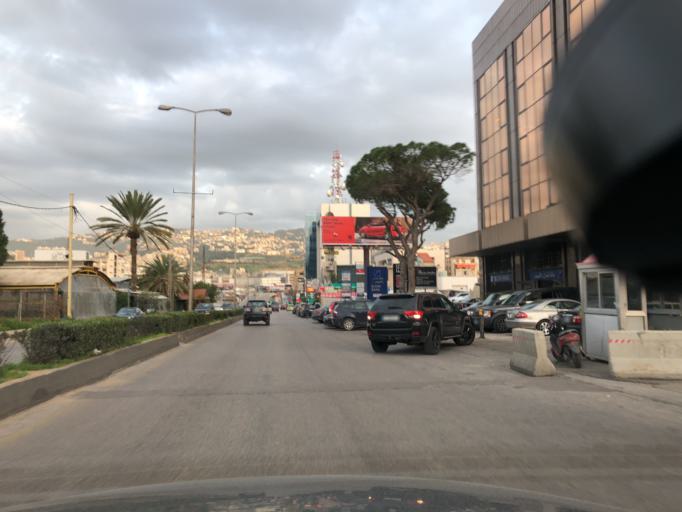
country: LB
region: Mont-Liban
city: Jdaidet el Matn
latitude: 33.8698
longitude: 35.5376
